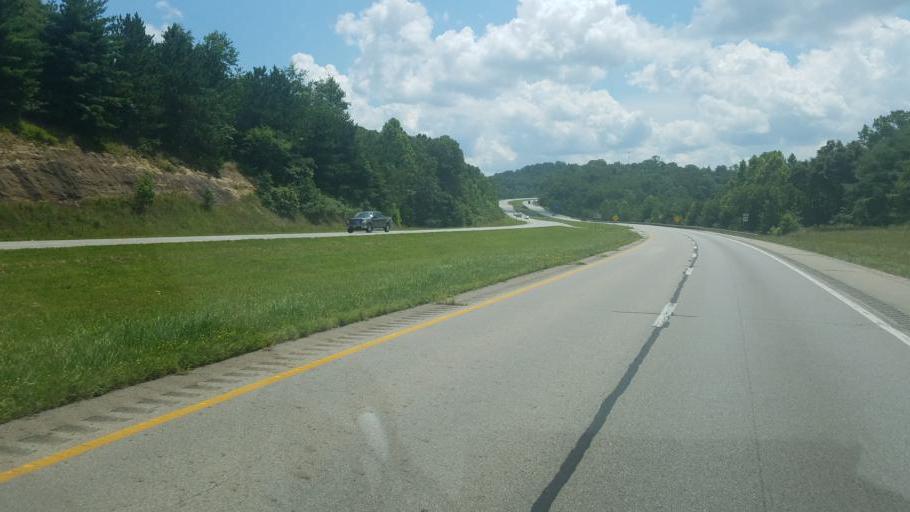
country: US
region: Ohio
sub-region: Jackson County
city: Jackson
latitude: 39.0665
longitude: -82.6252
